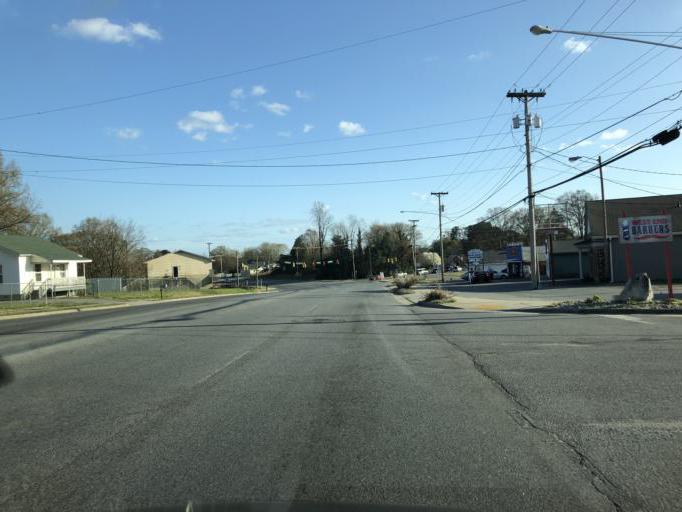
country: US
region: North Carolina
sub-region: Gaston County
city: Gastonia
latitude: 35.2694
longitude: -81.2225
